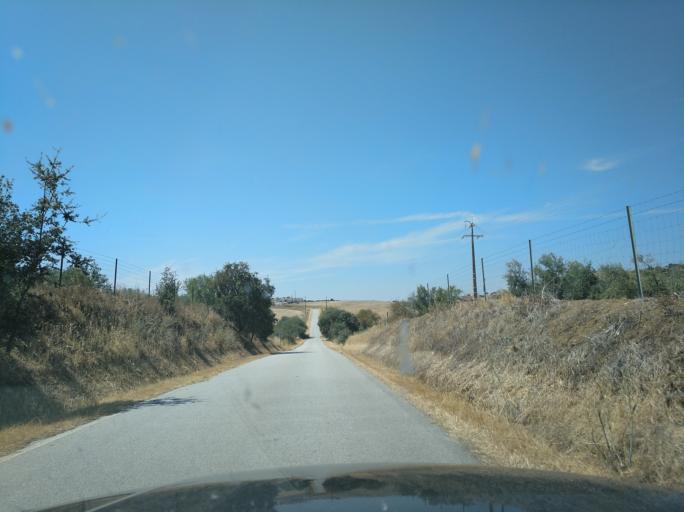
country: PT
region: Portalegre
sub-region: Campo Maior
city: Campo Maior
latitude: 38.9612
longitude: -7.1080
